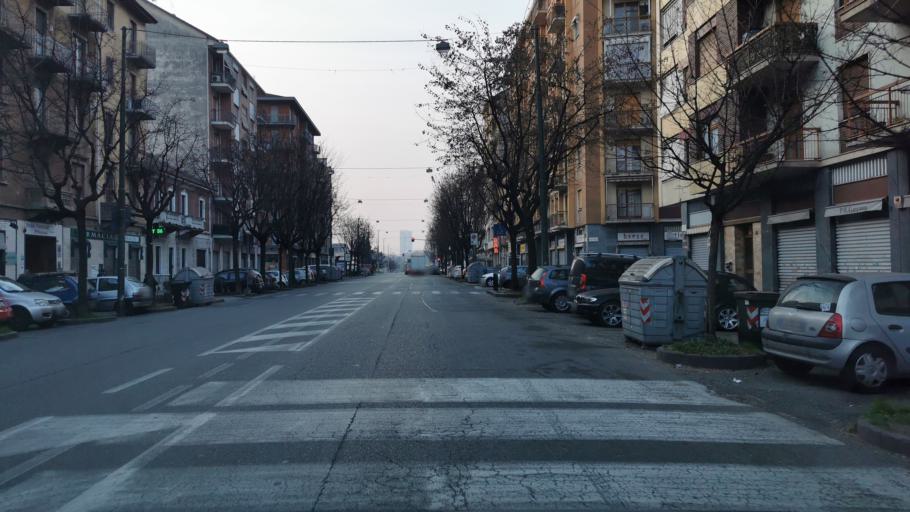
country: IT
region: Piedmont
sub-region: Provincia di Torino
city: Turin
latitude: 45.0971
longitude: 7.6630
